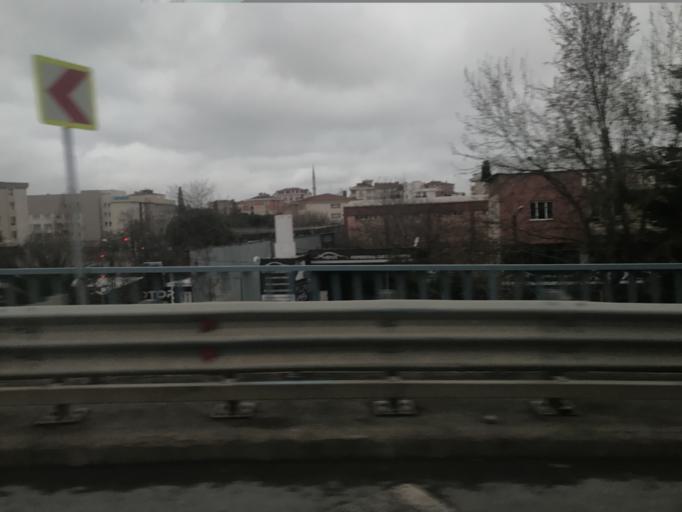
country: TR
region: Istanbul
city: Maltepe
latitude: 40.9139
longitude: 29.1699
